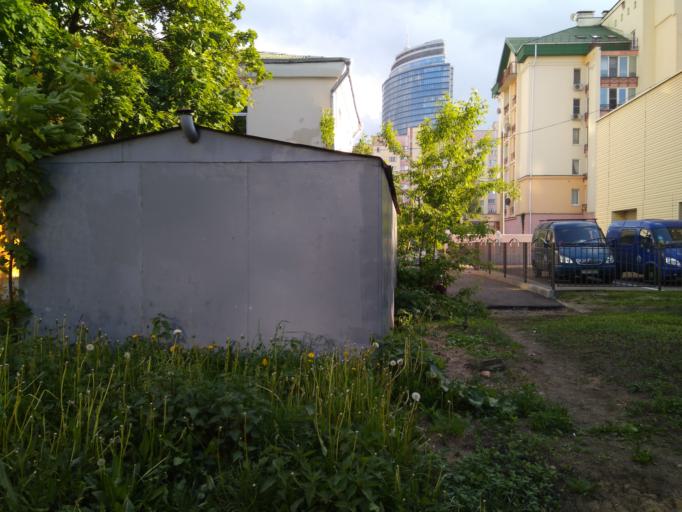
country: BY
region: Minsk
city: Minsk
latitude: 53.9096
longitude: 27.5344
